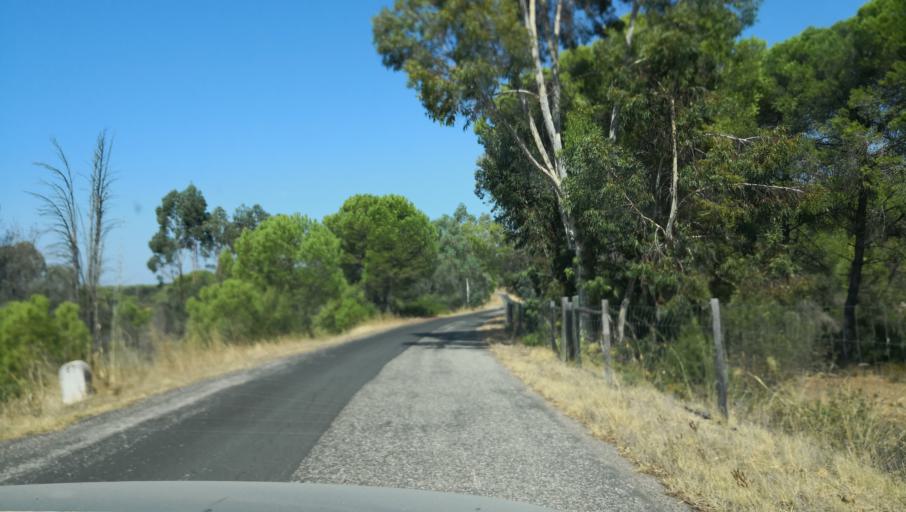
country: PT
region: Setubal
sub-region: Alcacer do Sal
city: Alcacer do Sal
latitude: 38.2501
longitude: -8.2972
